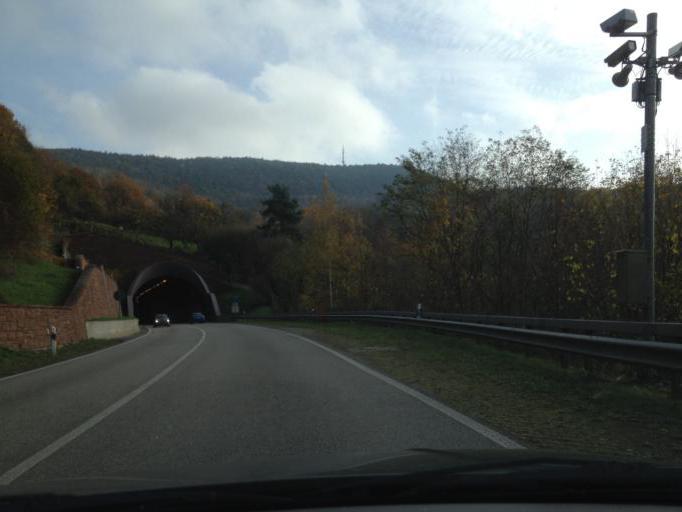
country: DE
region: Rheinland-Pfalz
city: Rinnthal
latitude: 49.2135
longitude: 7.9370
